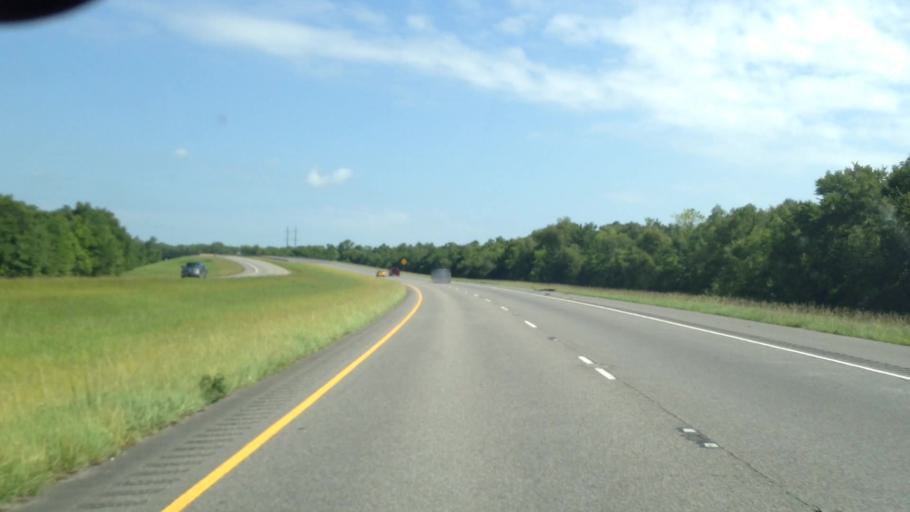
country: US
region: Louisiana
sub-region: Avoyelles Parish
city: Bunkie
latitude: 30.8936
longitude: -92.2268
